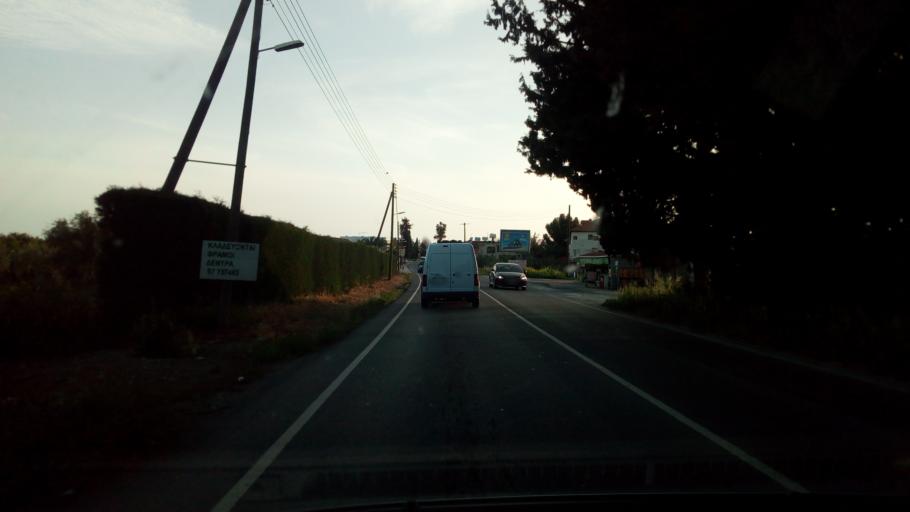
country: CY
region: Larnaka
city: Meneou
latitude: 34.8654
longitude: 33.5984
